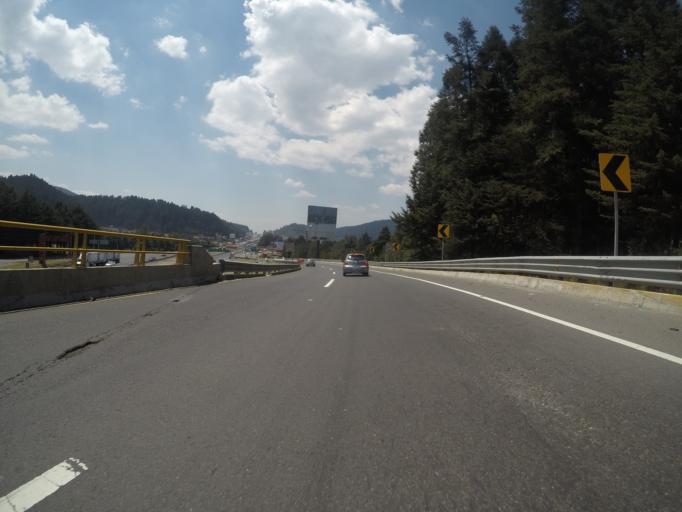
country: MX
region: Mexico
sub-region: Huixquilucan
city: El Palacio
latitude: 19.3014
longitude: -99.3761
